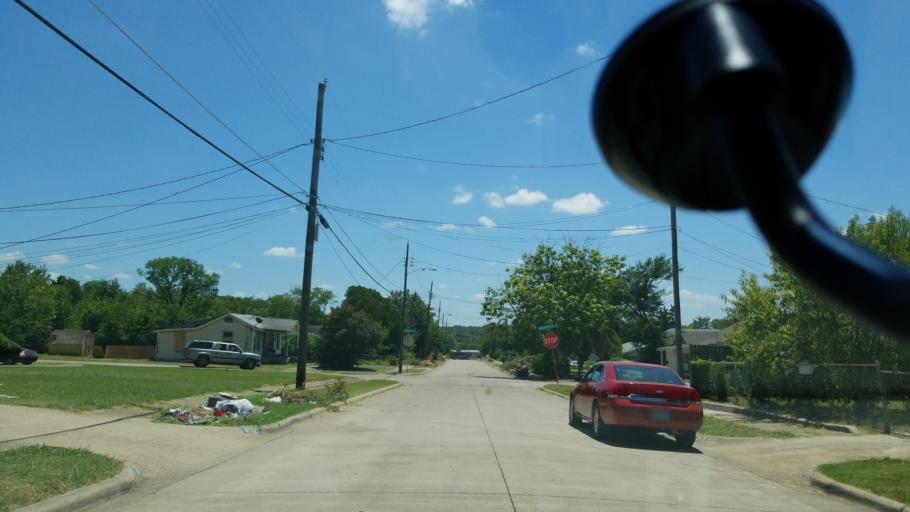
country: US
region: Texas
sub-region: Dallas County
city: Cockrell Hill
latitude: 32.6942
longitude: -96.8132
